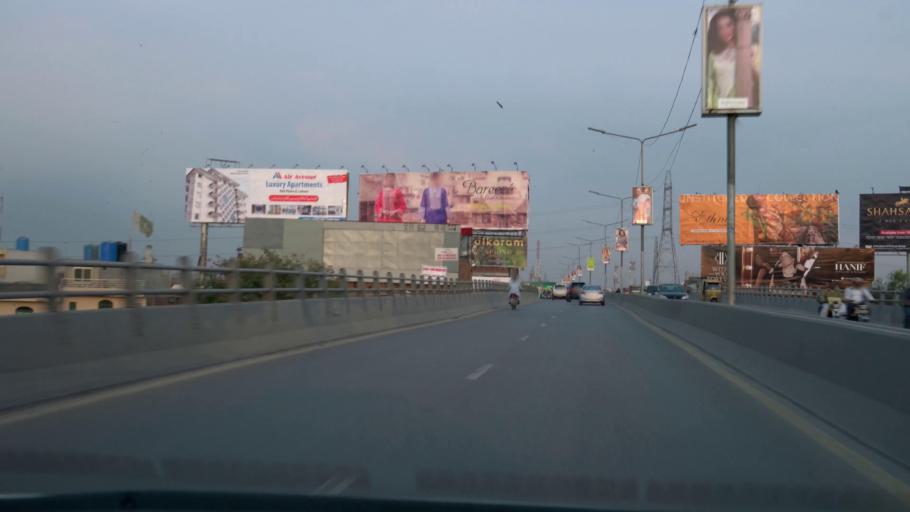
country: PK
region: Punjab
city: Lahore
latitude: 31.5022
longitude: 74.3553
